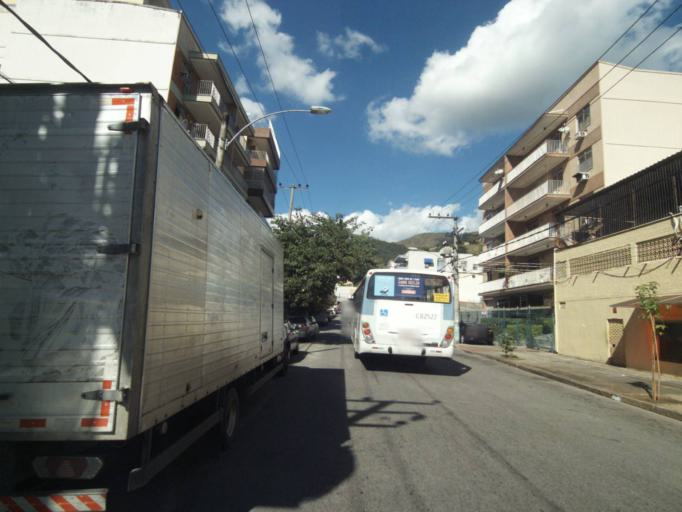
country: BR
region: Rio de Janeiro
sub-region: Rio De Janeiro
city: Rio de Janeiro
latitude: -22.9104
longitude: -43.2873
